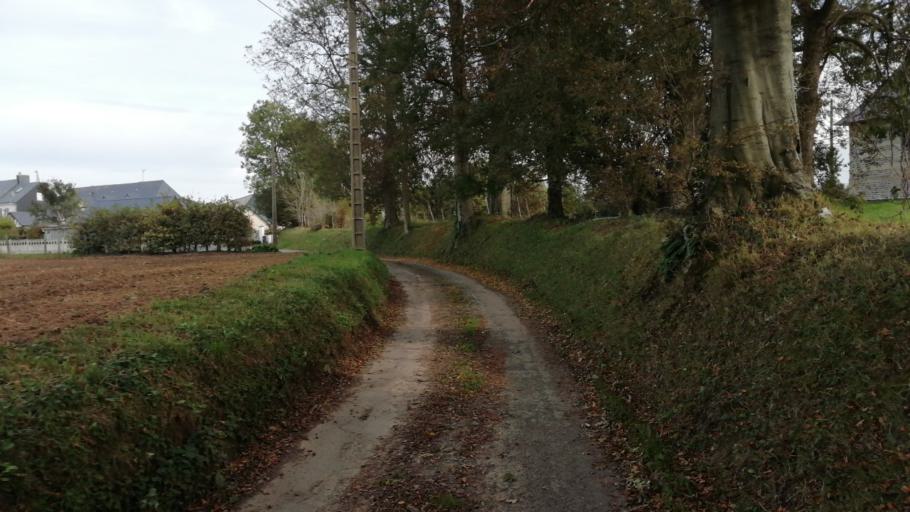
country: FR
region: Haute-Normandie
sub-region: Departement de la Seine-Maritime
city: Epouville
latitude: 49.5493
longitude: 0.2256
